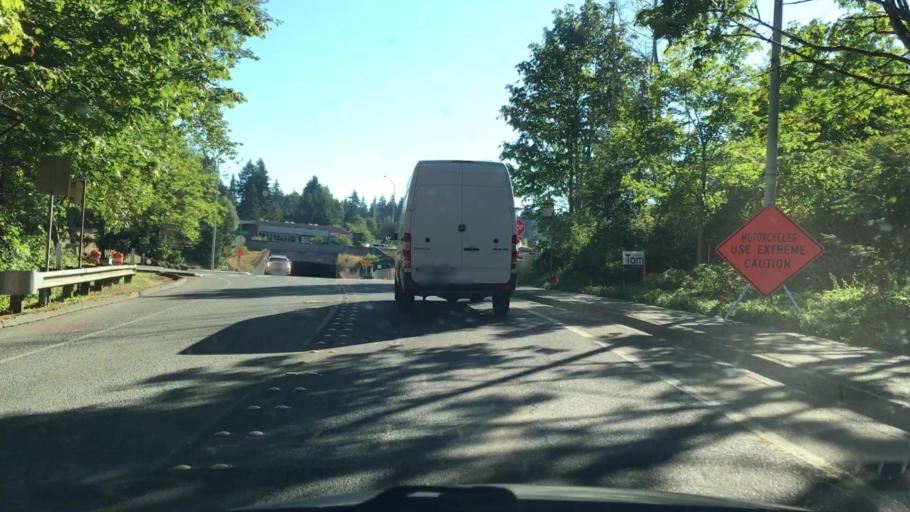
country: US
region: Washington
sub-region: King County
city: Eastgate
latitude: 47.5789
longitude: -122.1280
